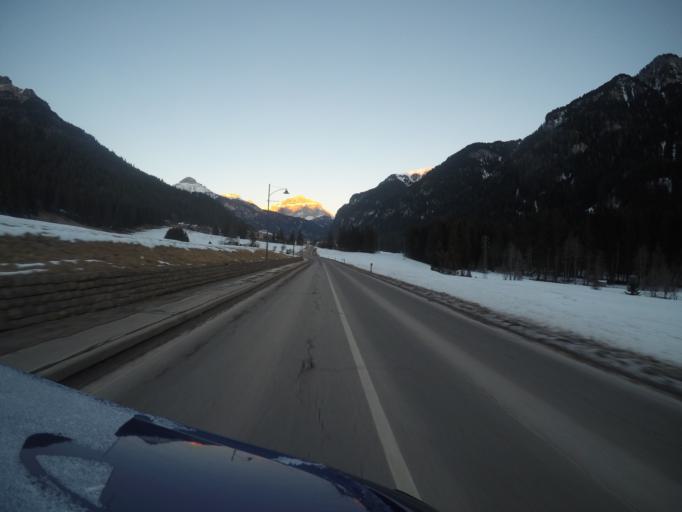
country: IT
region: Trentino-Alto Adige
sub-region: Provincia di Trento
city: Mazzin
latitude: 46.4606
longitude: 11.7067
